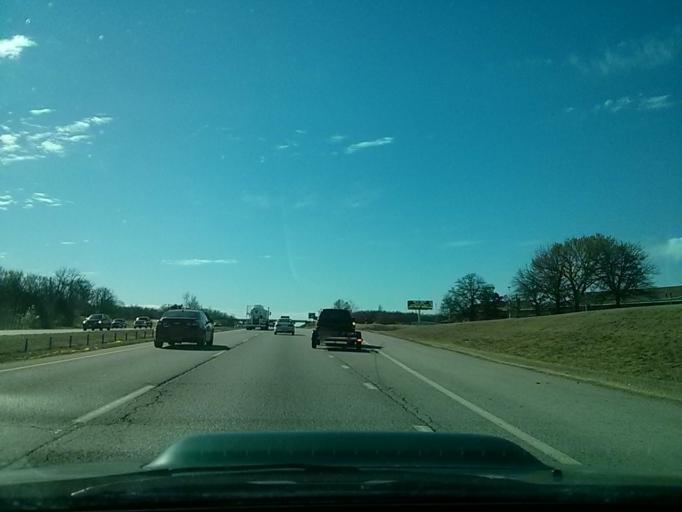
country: US
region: Oklahoma
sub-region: Tulsa County
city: Oakhurst
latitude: 36.0793
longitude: -96.0067
